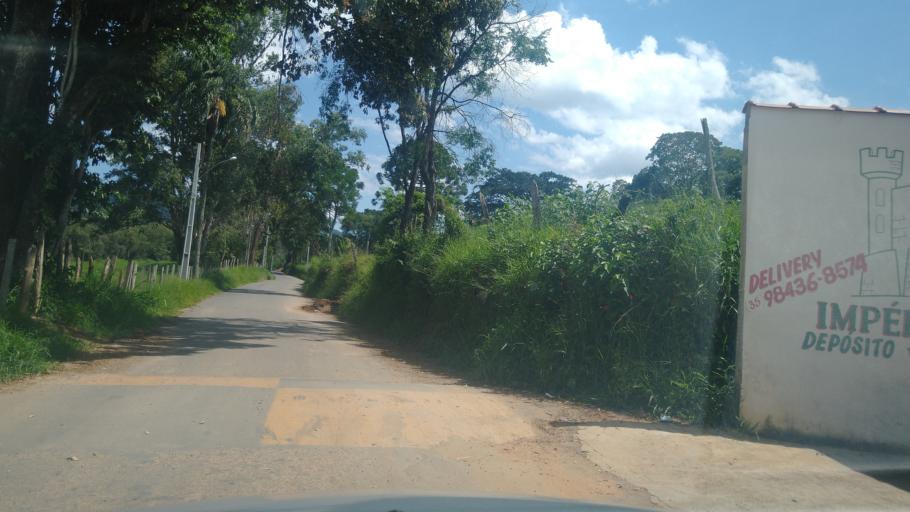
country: BR
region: Minas Gerais
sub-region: Extrema
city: Extrema
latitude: -22.7756
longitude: -46.2854
